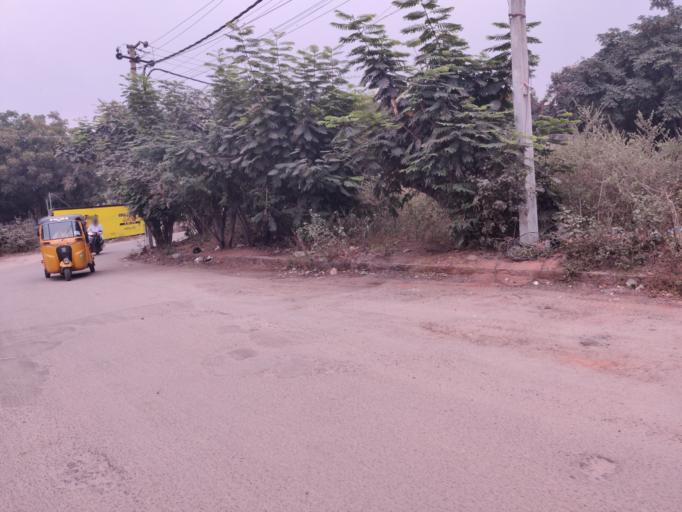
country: IN
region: Telangana
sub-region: Hyderabad
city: Hyderabad
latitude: 17.4070
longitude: 78.3955
